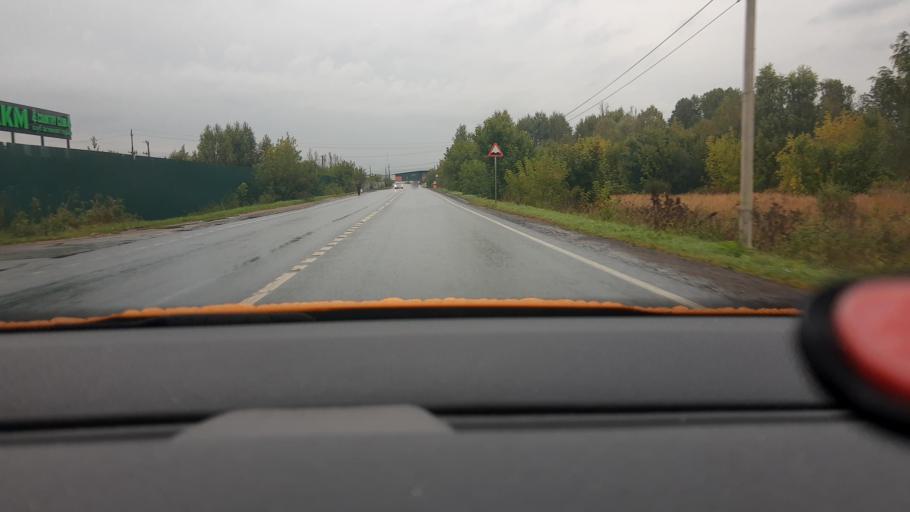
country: RU
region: Moskovskaya
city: Obukhovo
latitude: 55.8160
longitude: 38.2580
